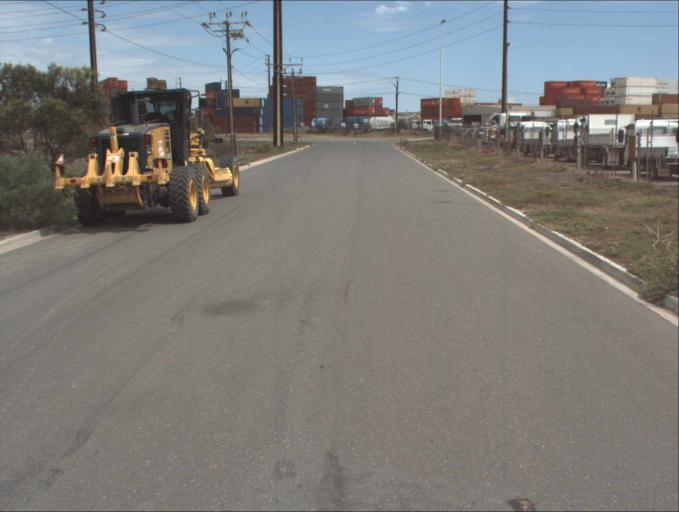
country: AU
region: South Australia
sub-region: Port Adelaide Enfield
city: Birkenhead
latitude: -34.8359
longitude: 138.5189
